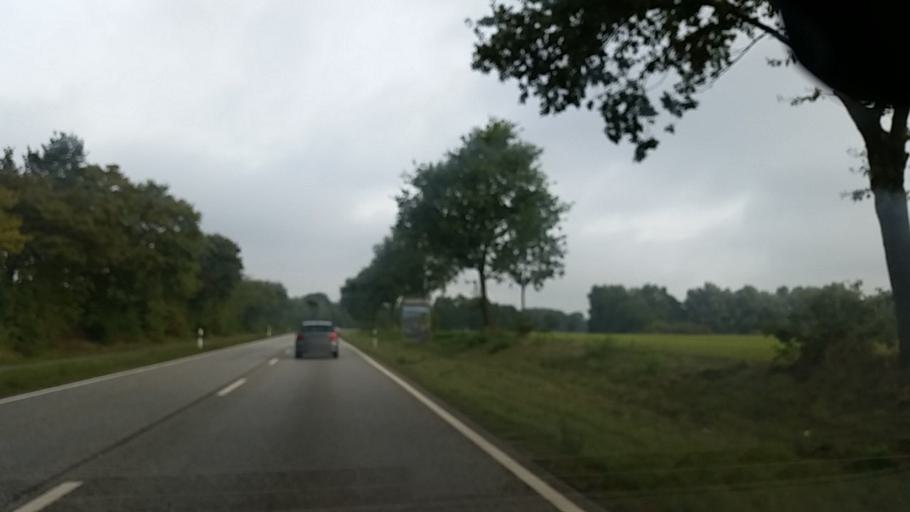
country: DE
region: Schleswig-Holstein
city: Norderstedt
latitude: 53.6945
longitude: 10.0088
